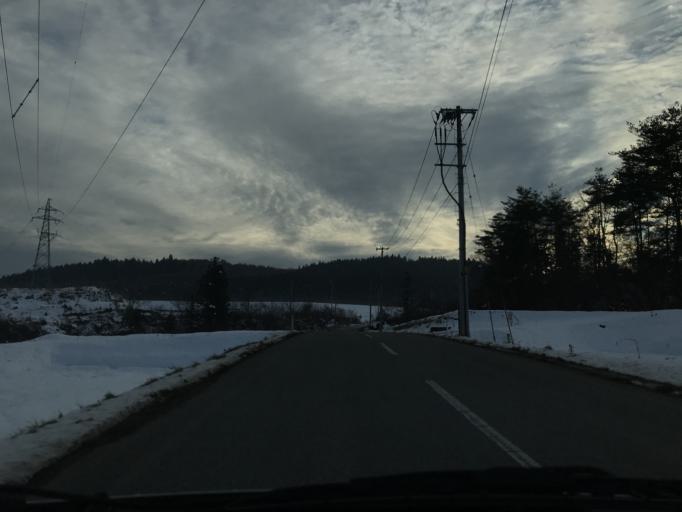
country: JP
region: Iwate
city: Mizusawa
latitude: 39.0538
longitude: 141.0822
